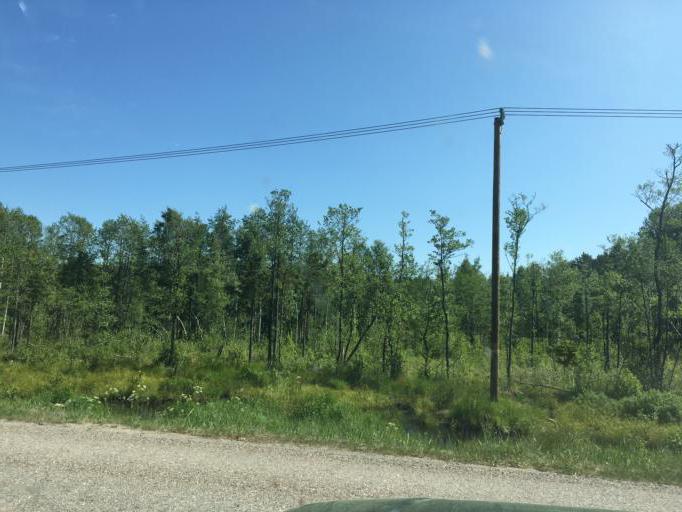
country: LV
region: Ventspils
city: Ventspils
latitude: 57.4597
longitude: 21.6549
